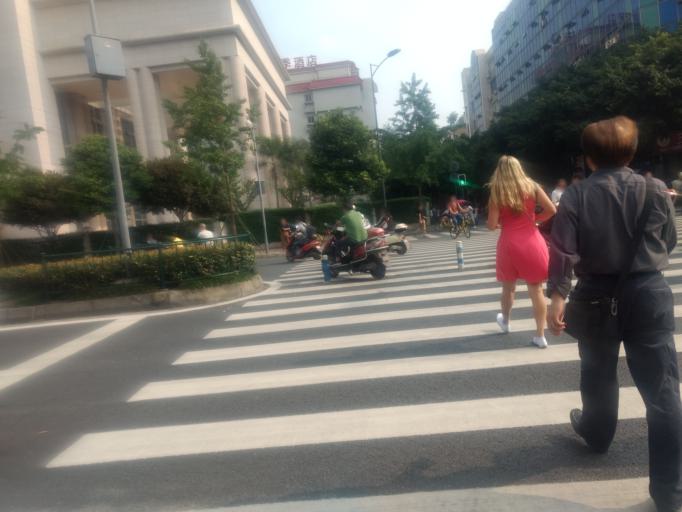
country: CN
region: Sichuan
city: Chengdu
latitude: 30.6738
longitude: 104.0682
